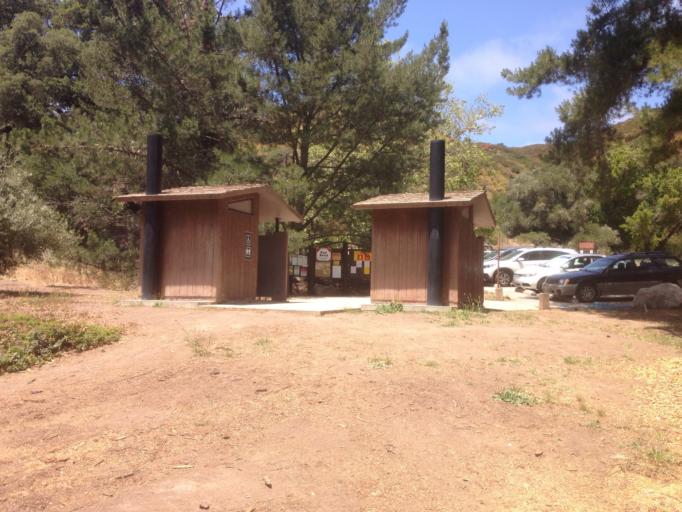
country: US
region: California
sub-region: San Luis Obispo County
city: Atascadero
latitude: 35.4248
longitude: -120.7406
